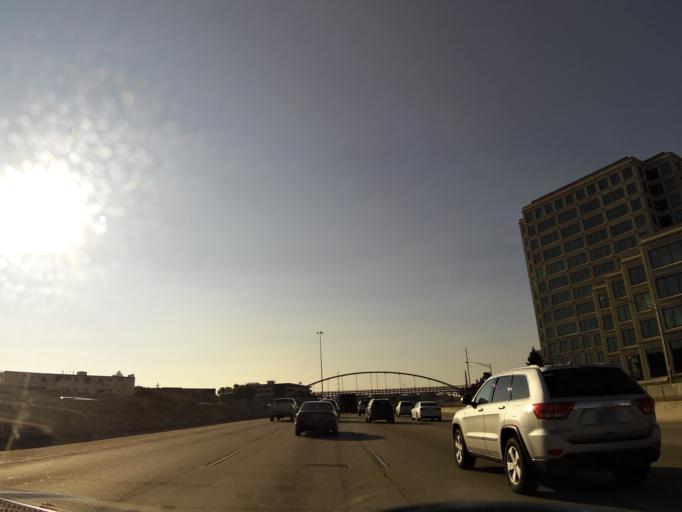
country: US
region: Colorado
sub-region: Arapahoe County
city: Glendale
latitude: 39.6816
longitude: -104.9374
